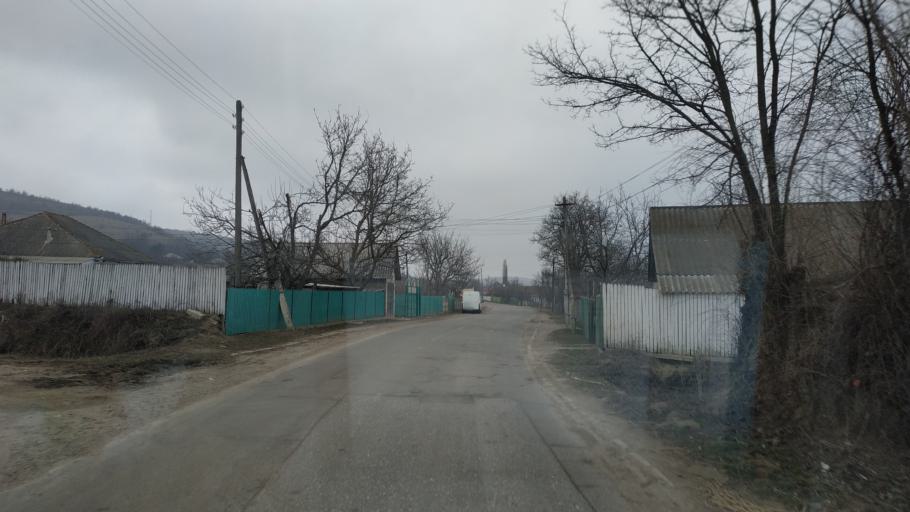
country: MD
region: Hincesti
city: Hincesti
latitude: 46.9820
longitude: 28.4514
